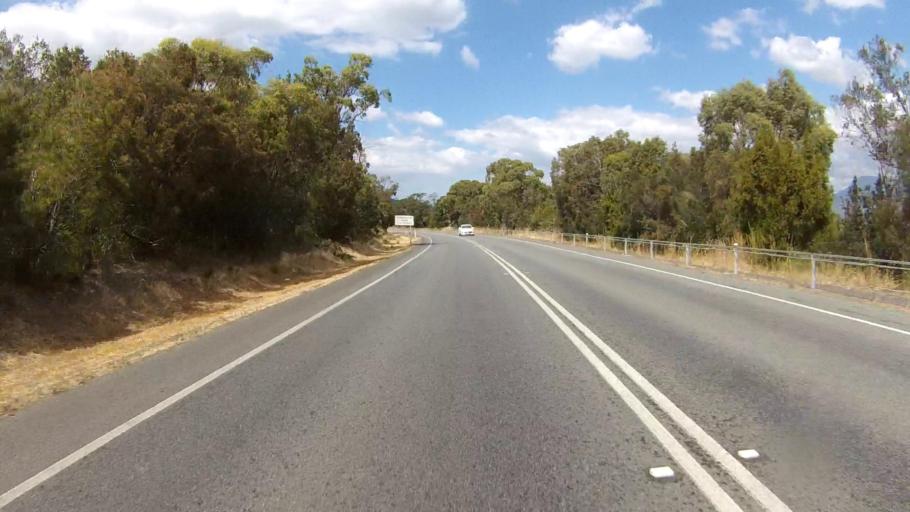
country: AU
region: Tasmania
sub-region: Brighton
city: Old Beach
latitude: -42.7757
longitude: 147.2699
